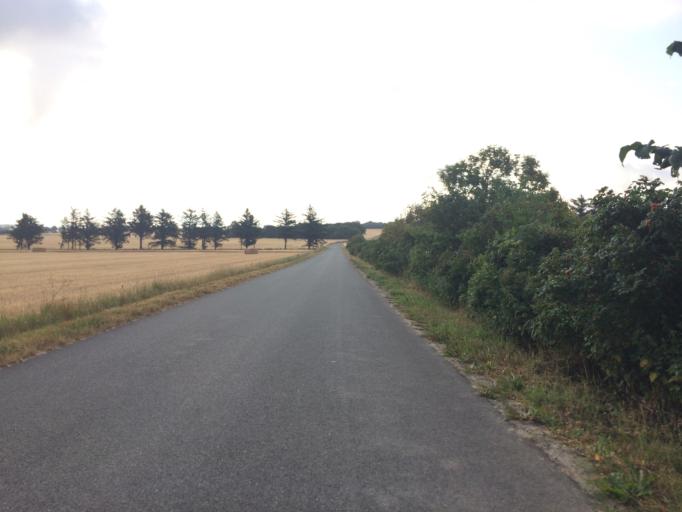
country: DK
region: Central Jutland
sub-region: Holstebro Kommune
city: Vinderup
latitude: 56.6042
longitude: 8.7113
